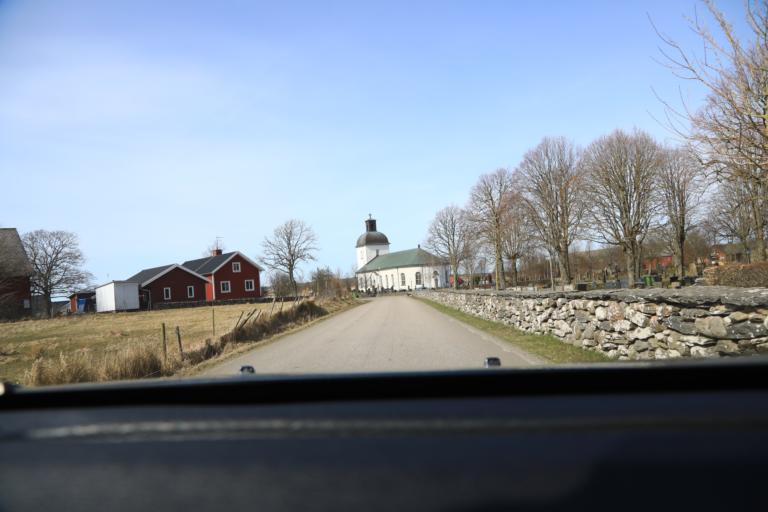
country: SE
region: Halland
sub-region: Kungsbacka Kommun
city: Frillesas
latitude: 57.2583
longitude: 12.1979
